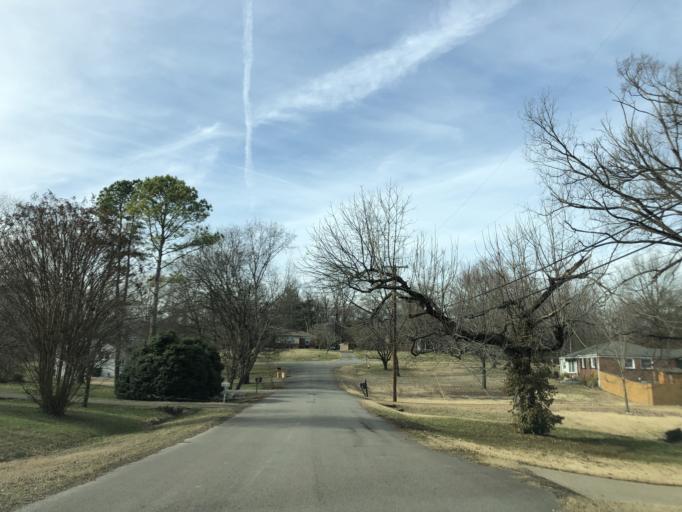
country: US
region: Tennessee
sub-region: Davidson County
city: Nashville
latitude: 36.2170
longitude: -86.7340
